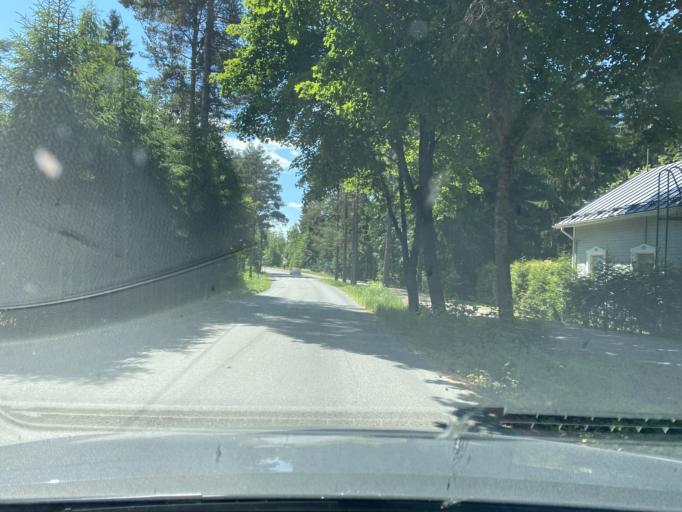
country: FI
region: Satakunta
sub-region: Rauma
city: Eura
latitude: 61.1297
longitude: 22.1654
